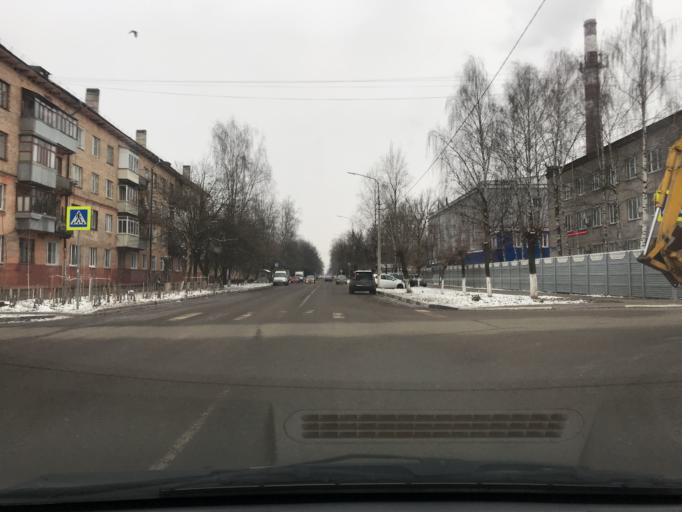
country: RU
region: Moskovskaya
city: Elektrostal'
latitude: 55.7885
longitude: 38.4479
